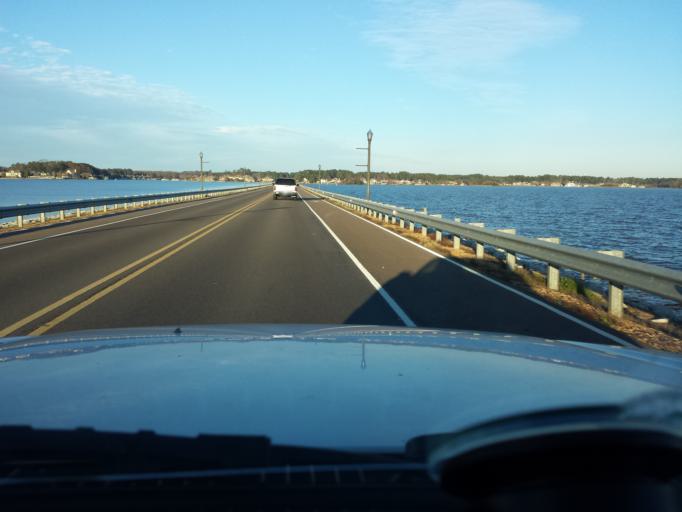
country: US
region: Mississippi
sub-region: Madison County
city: Madison
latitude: 32.3974
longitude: -90.0244
